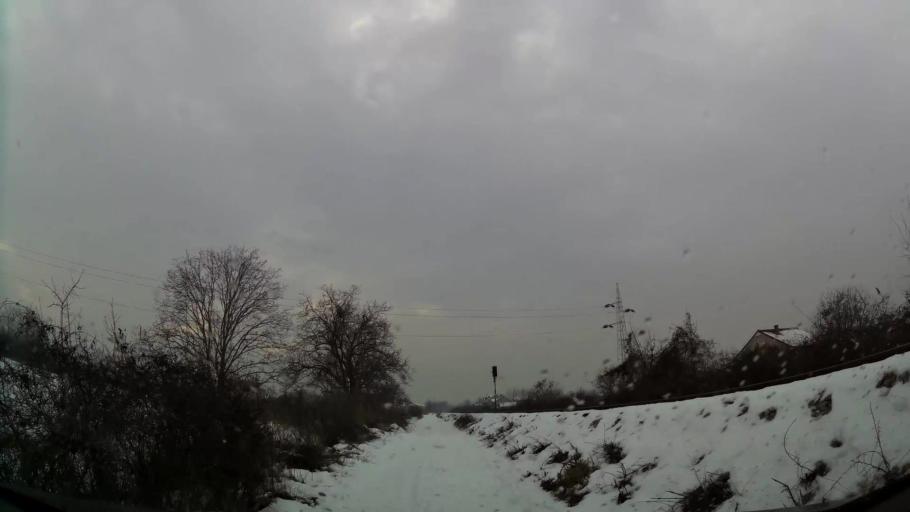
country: MK
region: Saraj
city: Saraj
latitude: 42.0401
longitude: 21.3523
